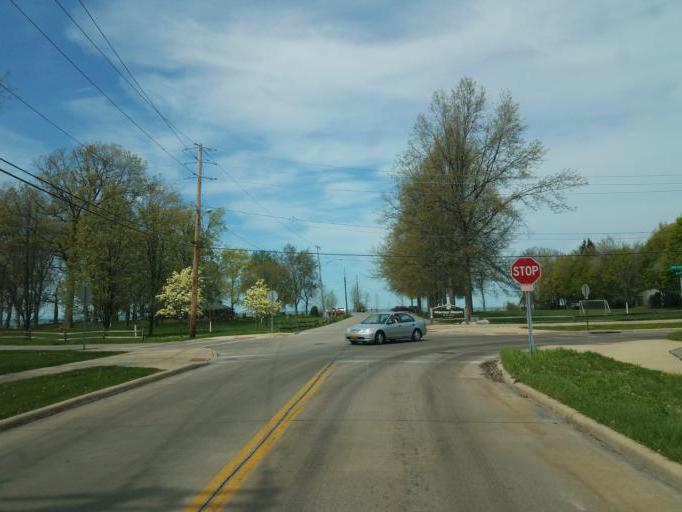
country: US
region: Ohio
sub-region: Lake County
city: Mentor-on-the-Lake
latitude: 41.7194
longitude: -81.3614
